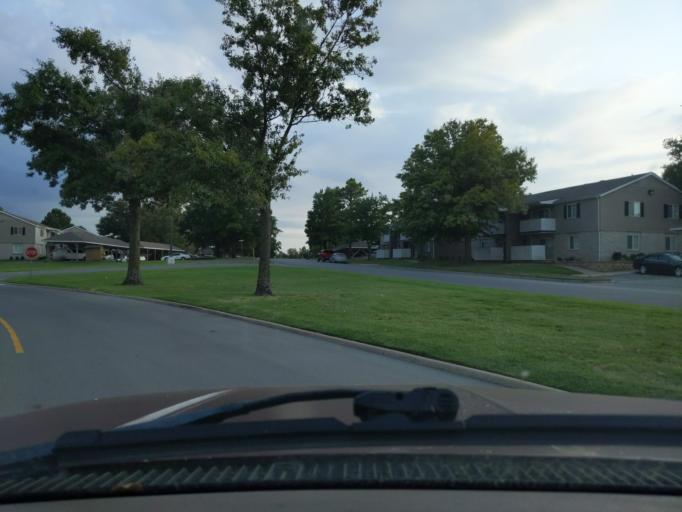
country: US
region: Oklahoma
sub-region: Tulsa County
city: Broken Arrow
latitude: 36.1305
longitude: -95.8232
